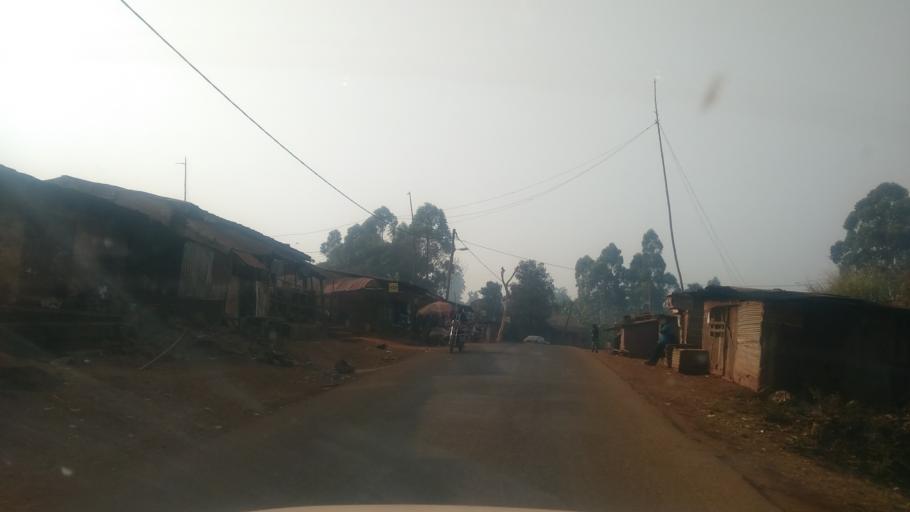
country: CM
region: West
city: Bandjoun
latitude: 5.3462
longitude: 10.4051
